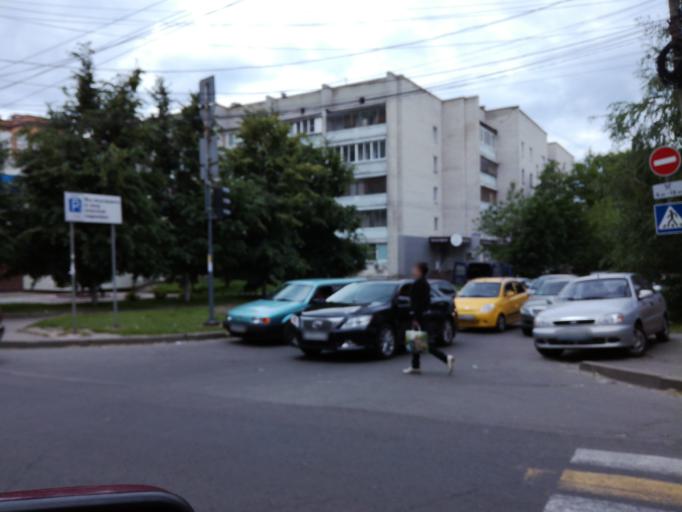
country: RU
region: Kursk
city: Kursk
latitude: 51.7347
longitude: 36.1902
